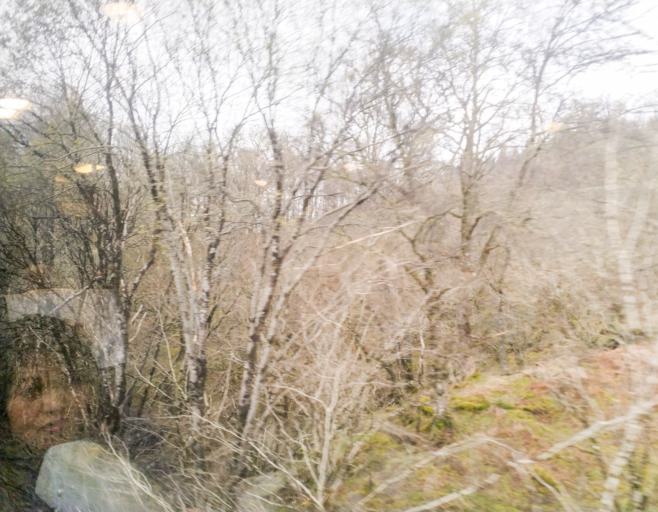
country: GB
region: Scotland
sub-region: Highland
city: Spean Bridge
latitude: 56.8862
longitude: -4.8012
